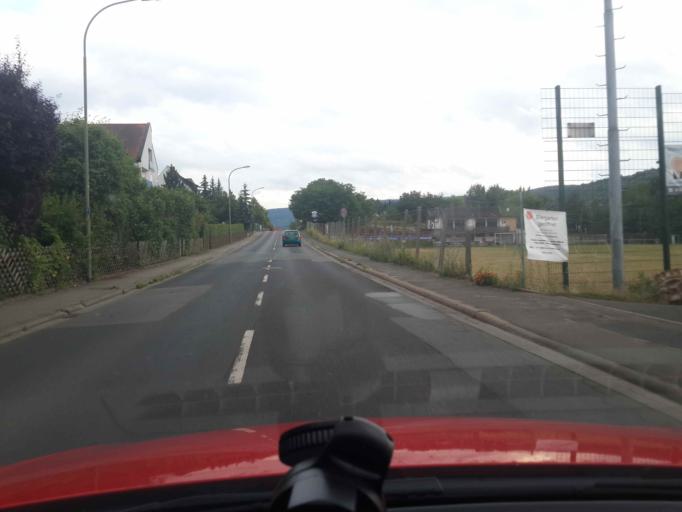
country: DE
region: Bavaria
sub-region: Regierungsbezirk Unterfranken
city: Klingenberg am Main
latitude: 49.7726
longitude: 9.1842
